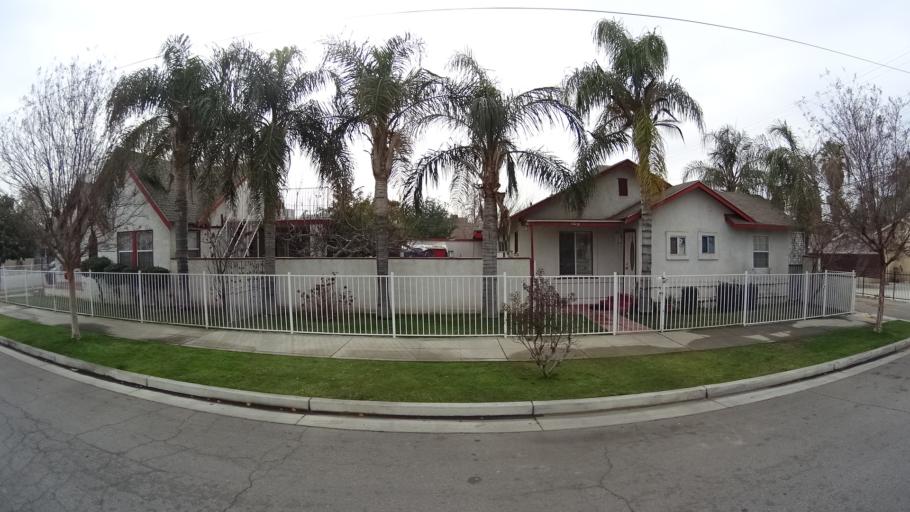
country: US
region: California
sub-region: Kern County
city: Bakersfield
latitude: 35.3665
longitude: -119.0169
